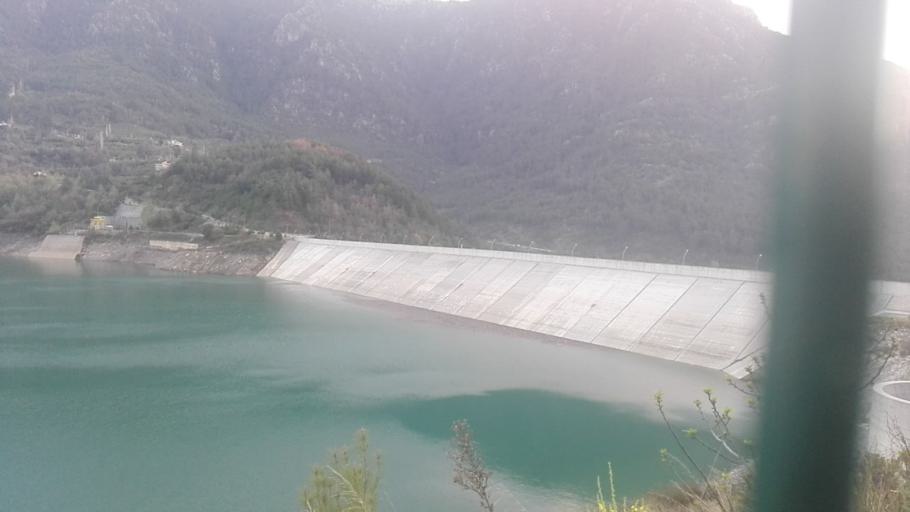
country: TR
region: Antalya
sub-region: Alanya
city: Mahmutlar
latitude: 36.5540
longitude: 32.1404
